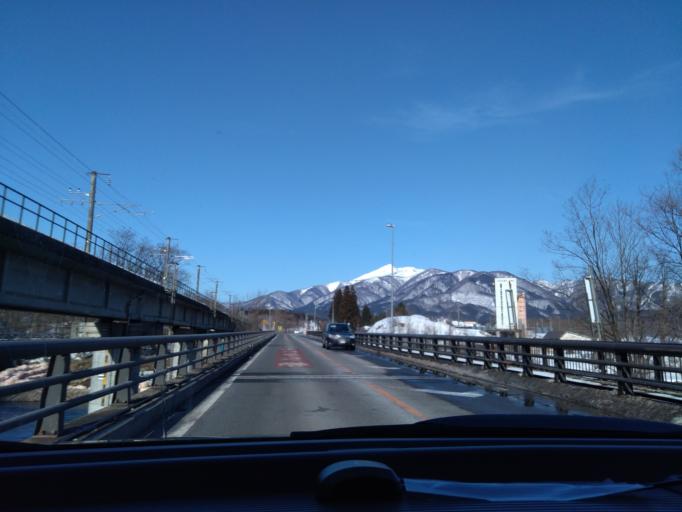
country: JP
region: Akita
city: Kakunodatemachi
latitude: 39.6864
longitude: 140.7076
